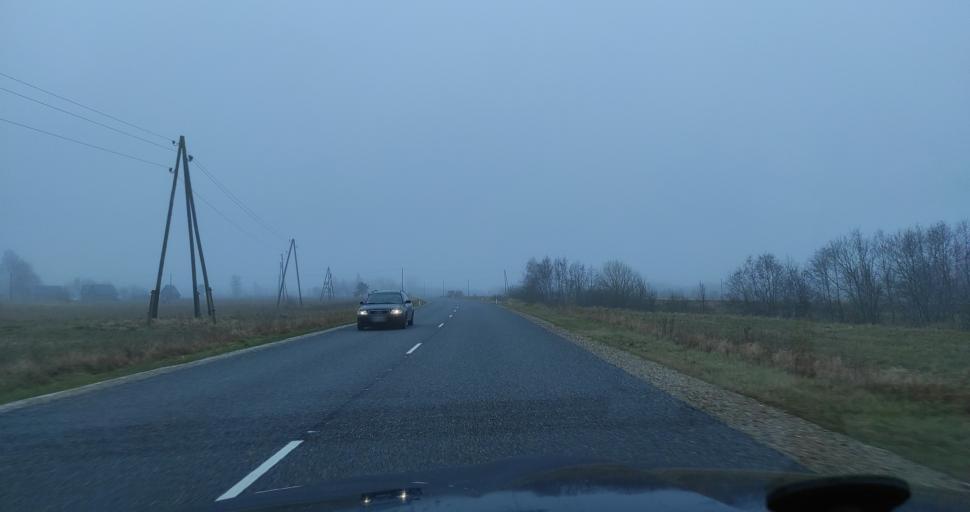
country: LV
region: Alsunga
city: Alsunga
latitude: 56.9850
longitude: 21.3604
